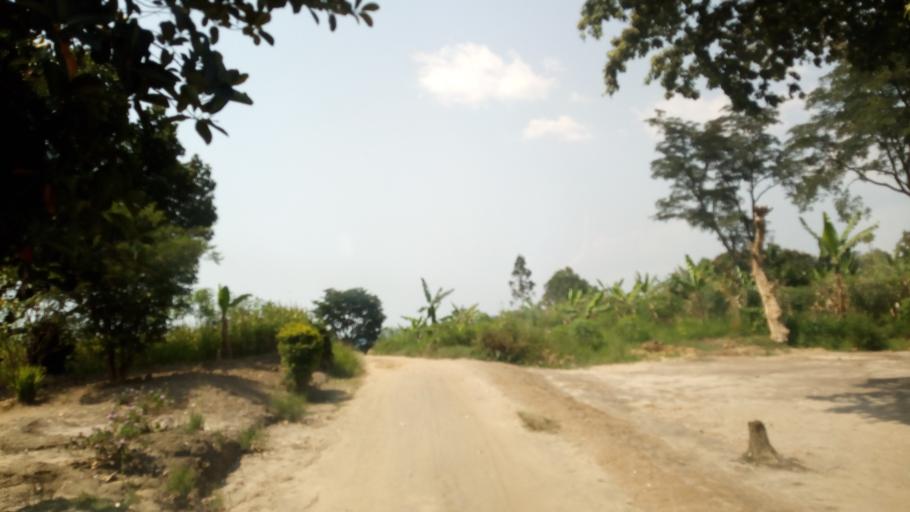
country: UG
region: Western Region
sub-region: Kanungu District
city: Ntungamo
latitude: -0.8043
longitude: 29.6496
